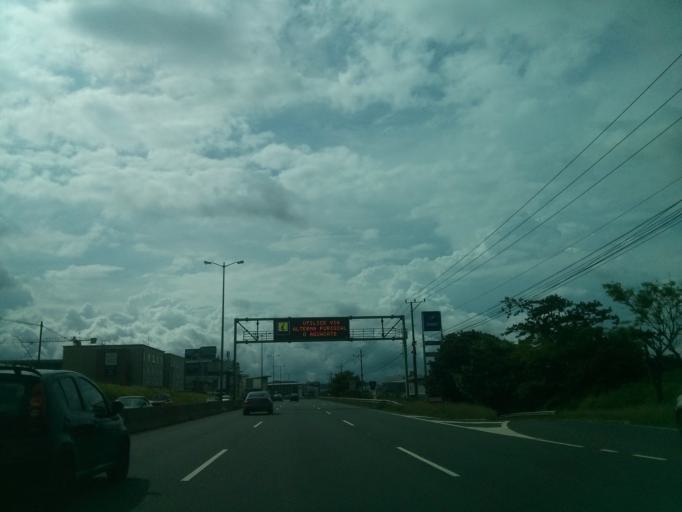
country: CR
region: San Jose
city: San Rafael
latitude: 9.9387
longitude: -84.1388
